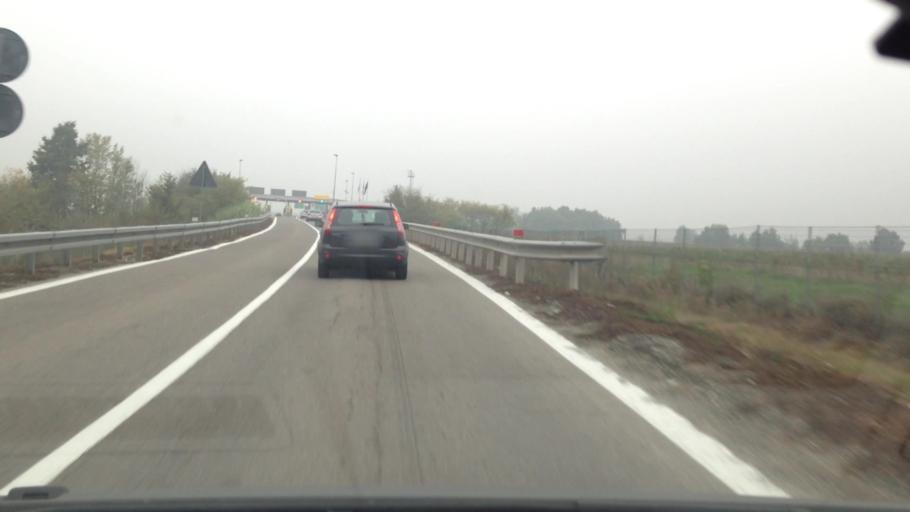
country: IT
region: Piedmont
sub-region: Provincia di Alessandria
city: Quattordio
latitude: 44.9066
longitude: 8.4114
